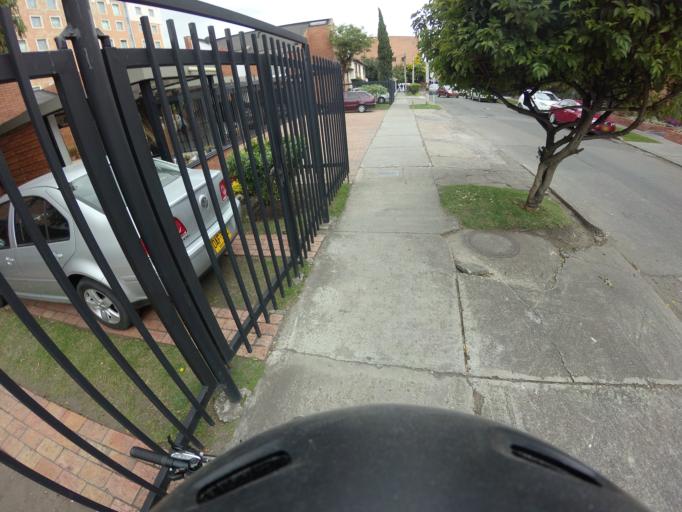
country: CO
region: Bogota D.C.
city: Barrio San Luis
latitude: 4.7070
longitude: -74.0509
